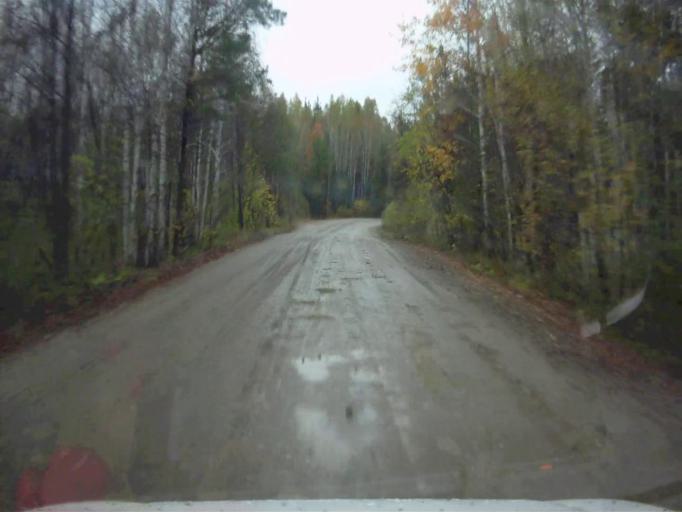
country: RU
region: Chelyabinsk
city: Kyshtym
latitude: 55.8338
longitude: 60.4858
